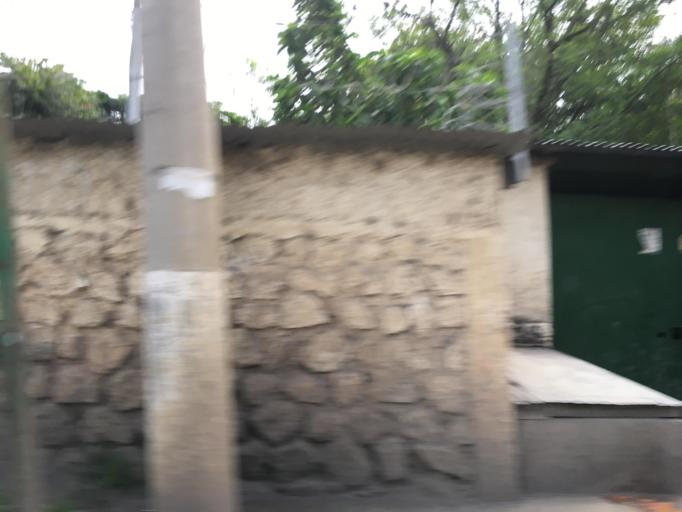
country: GT
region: Guatemala
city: Amatitlan
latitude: 14.4741
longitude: -90.6074
